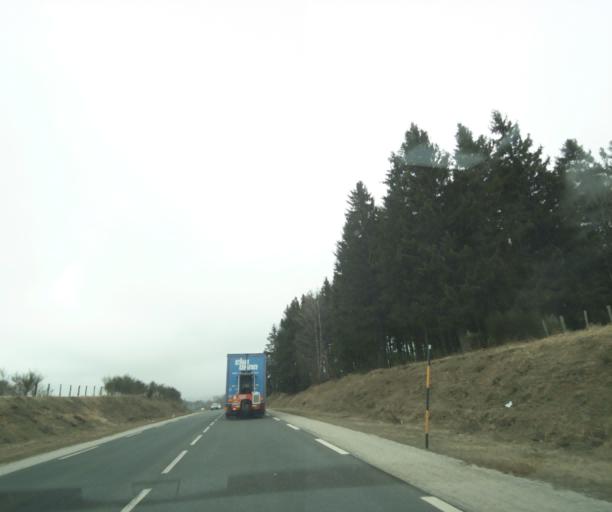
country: FR
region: Languedoc-Roussillon
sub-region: Departement de la Lozere
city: Langogne
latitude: 44.7064
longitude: 3.8209
